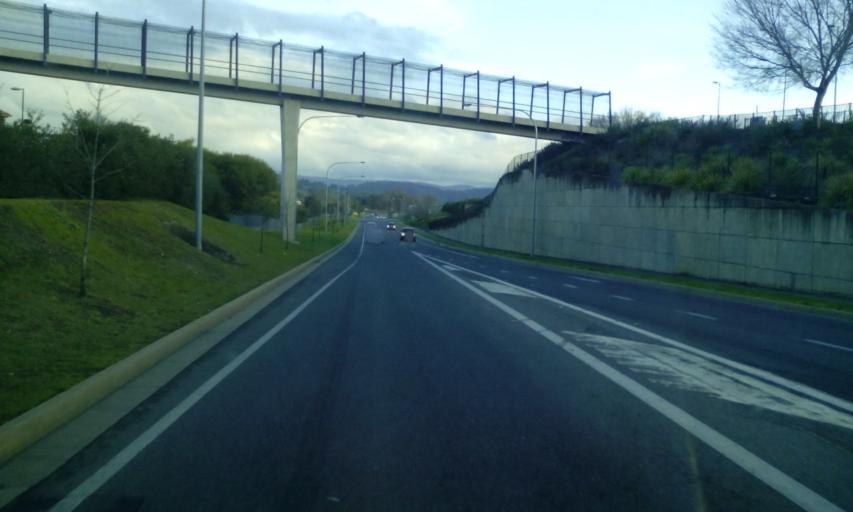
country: AU
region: New South Wales
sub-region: Albury Municipality
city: East Albury
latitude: -36.0870
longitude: 146.9236
